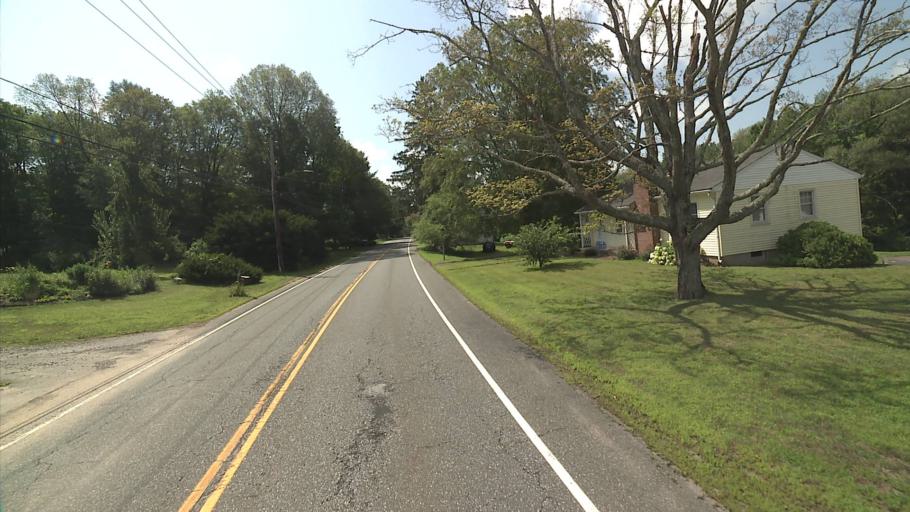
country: US
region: Connecticut
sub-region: Middlesex County
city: Deep River Center
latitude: 41.3674
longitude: -72.4509
